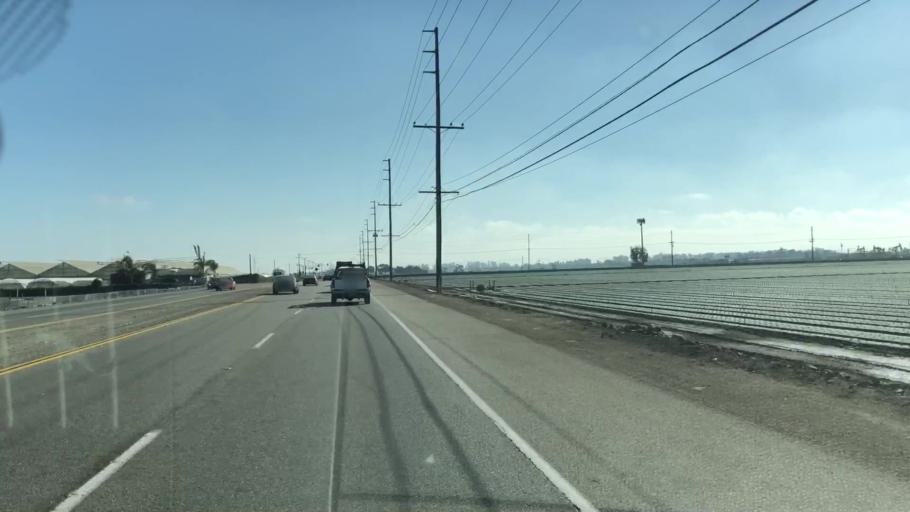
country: US
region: California
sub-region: Ventura County
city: Oxnard
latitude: 34.1937
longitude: -119.1424
